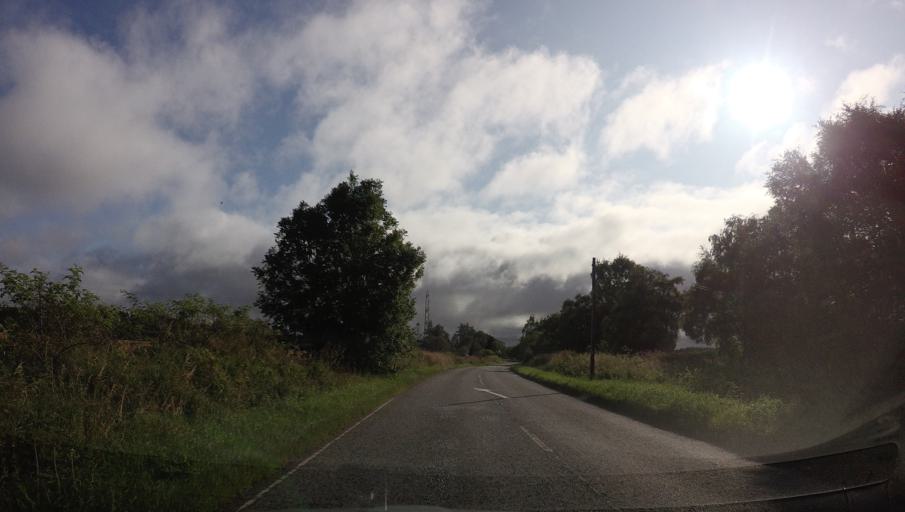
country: GB
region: Scotland
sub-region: Aberdeenshire
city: Banchory
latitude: 57.0627
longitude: -2.3956
